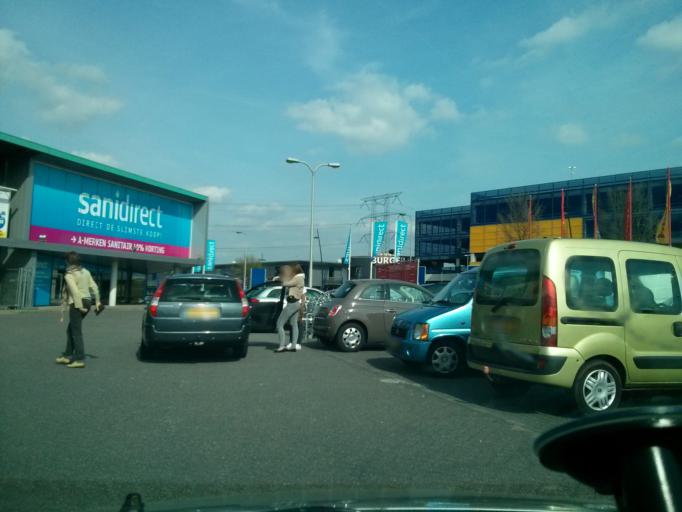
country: NL
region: North Brabant
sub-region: Gemeente Son en Breugel
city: Son
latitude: 51.4997
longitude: 5.4711
